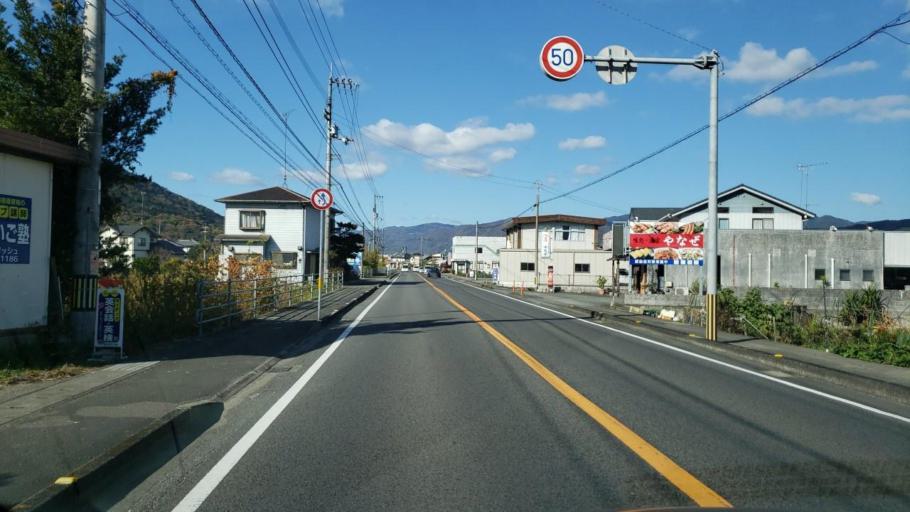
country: JP
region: Tokushima
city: Wakimachi
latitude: 34.0593
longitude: 134.2177
